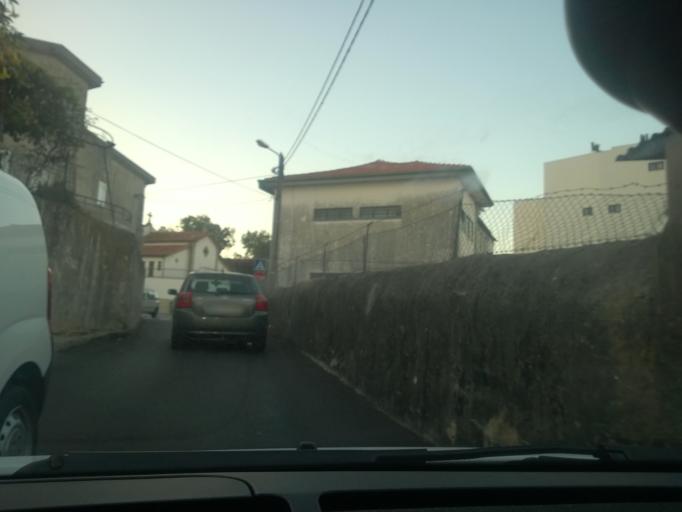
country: PT
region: Porto
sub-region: Vila Nova de Gaia
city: Oliveira do Douro
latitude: 41.1041
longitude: -8.5724
